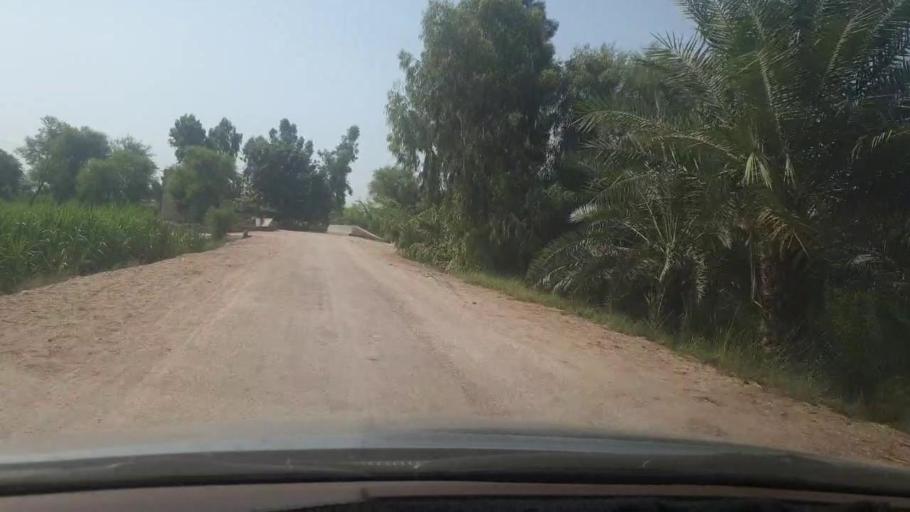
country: PK
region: Sindh
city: Ranipur
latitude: 27.2824
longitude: 68.5812
